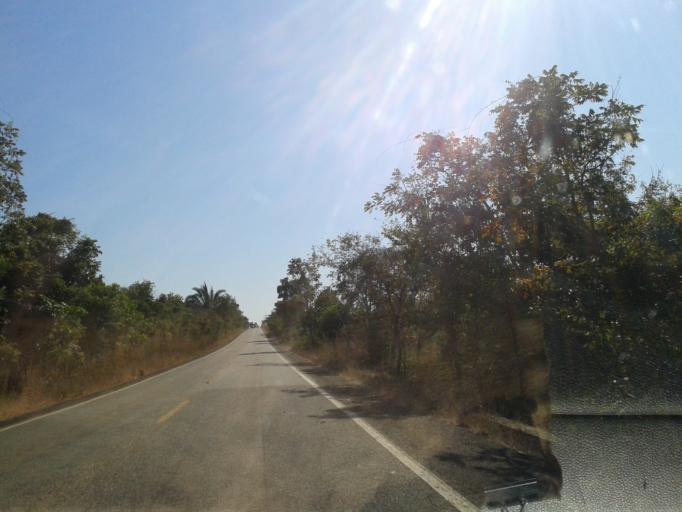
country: BR
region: Goias
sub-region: Mozarlandia
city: Mozarlandia
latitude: -14.5394
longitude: -50.4892
